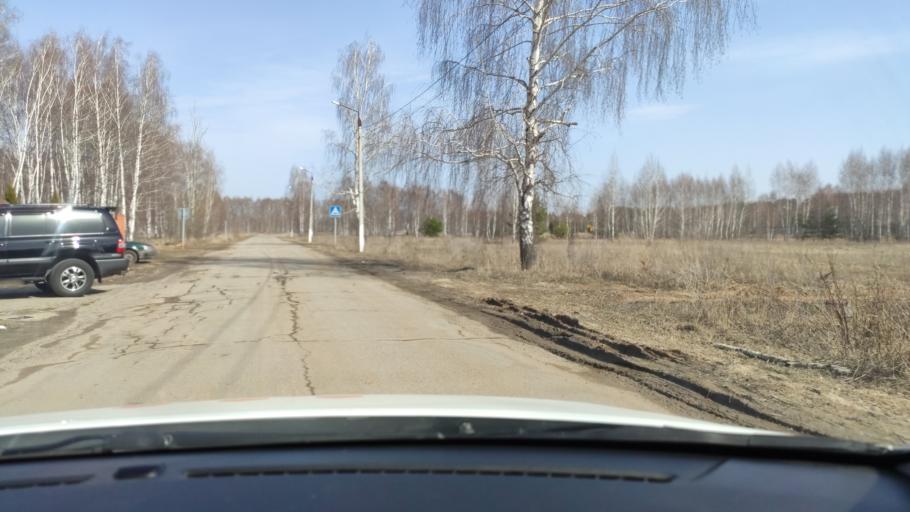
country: RU
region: Tatarstan
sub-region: Gorod Kazan'
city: Kazan
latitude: 55.6916
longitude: 49.1167
